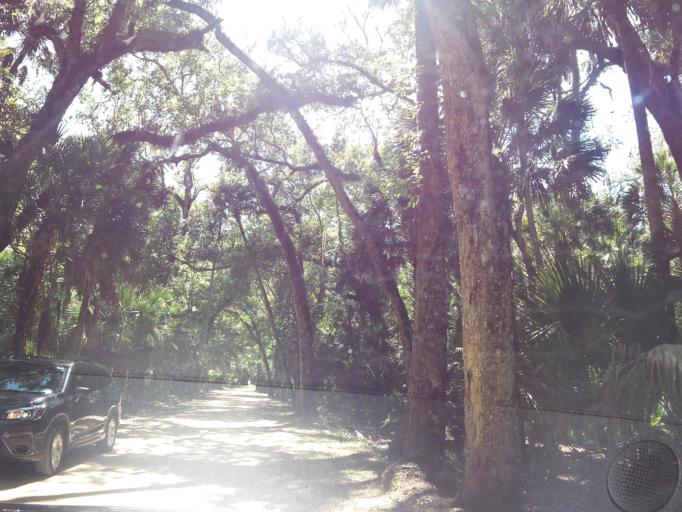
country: US
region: Florida
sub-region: Flagler County
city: Flagler Beach
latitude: 29.4331
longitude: -81.1428
